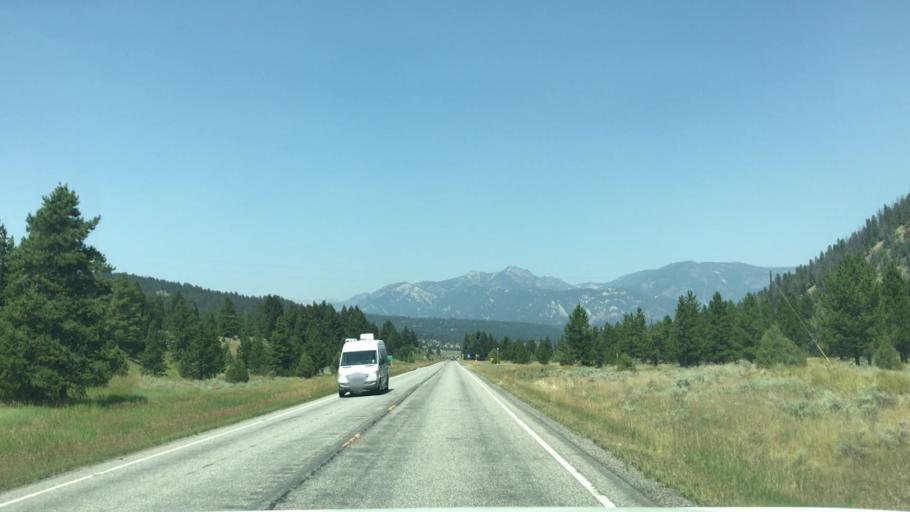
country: US
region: Montana
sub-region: Gallatin County
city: Big Sky
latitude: 45.2059
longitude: -111.2429
